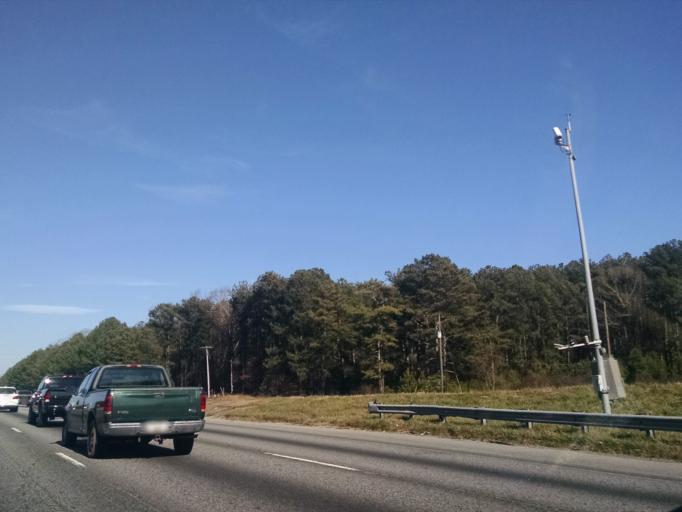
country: US
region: Georgia
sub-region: Gwinnett County
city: Suwanee
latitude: 34.0383
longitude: -84.0375
